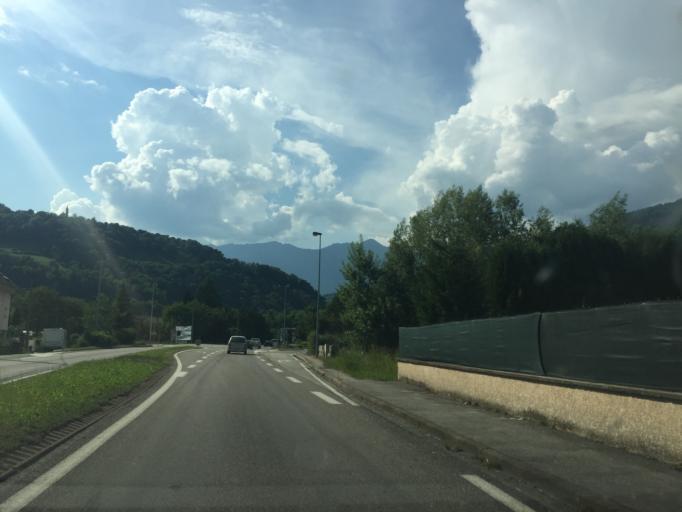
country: FR
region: Rhone-Alpes
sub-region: Departement de la Savoie
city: Aiton
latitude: 45.5446
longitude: 6.2991
